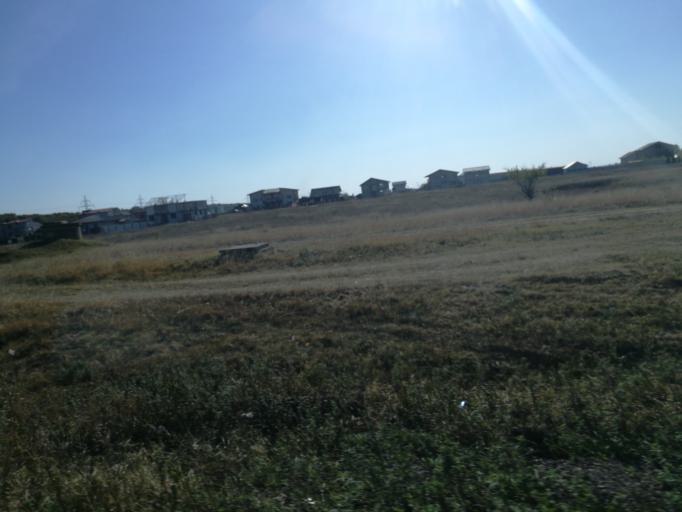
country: RO
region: Giurgiu
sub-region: Comuna Joita
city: Bacu
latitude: 44.4747
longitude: 25.9091
